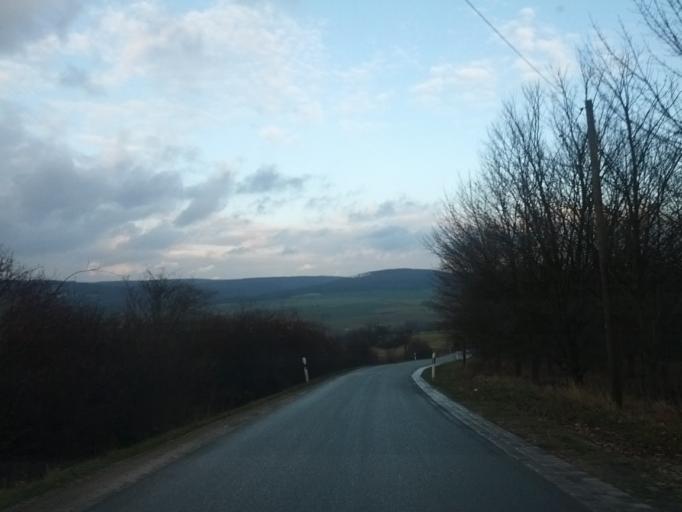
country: DE
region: Thuringia
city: Bischofroda
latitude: 51.0453
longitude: 10.3546
